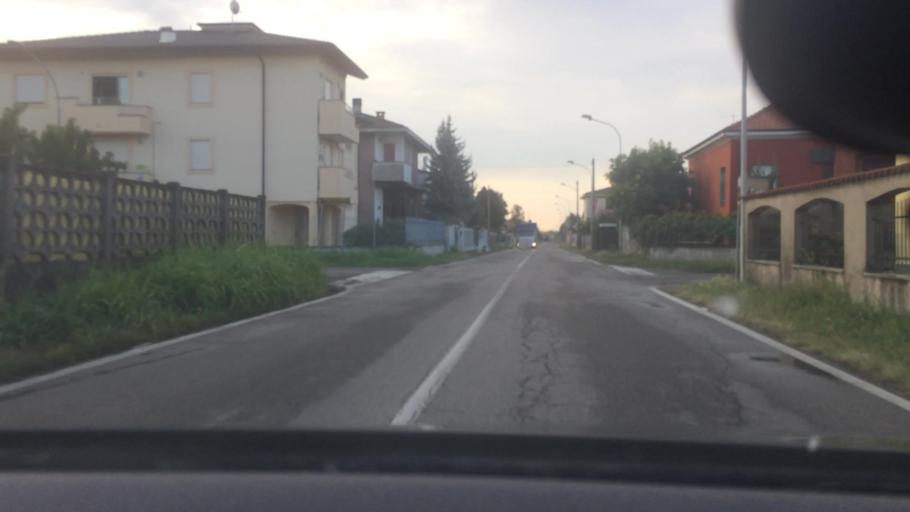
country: IT
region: Lombardy
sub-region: Citta metropolitana di Milano
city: Busto Garolfo
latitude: 45.5491
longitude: 8.8915
